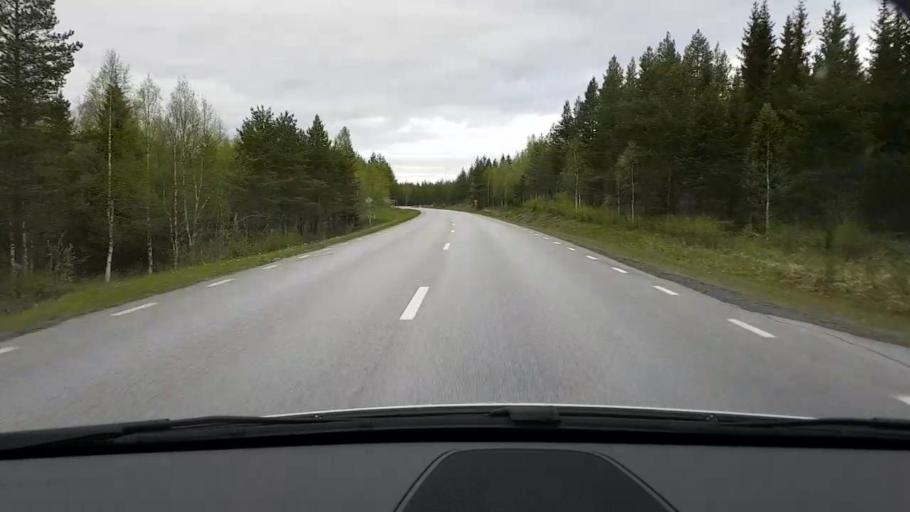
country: SE
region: Jaemtland
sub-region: Krokoms Kommun
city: Valla
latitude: 63.3059
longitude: 13.9229
